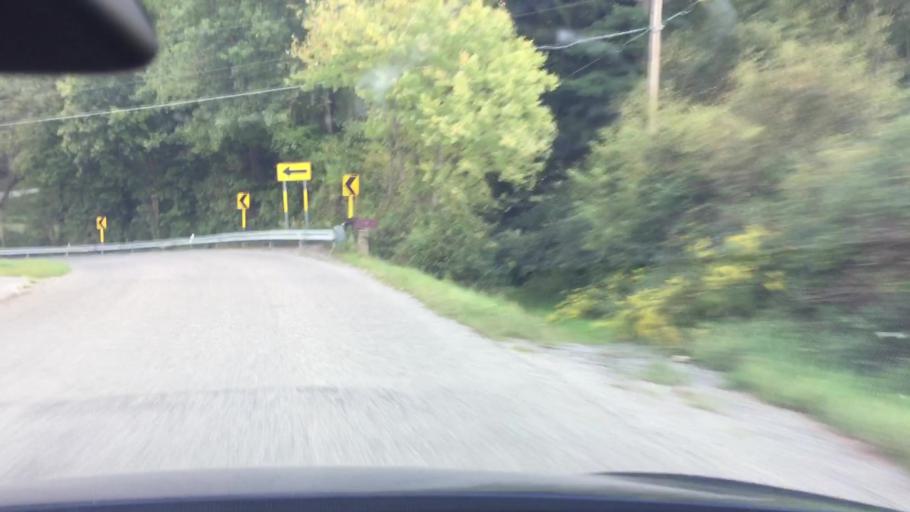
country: US
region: Pennsylvania
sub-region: Butler County
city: Oak Hills
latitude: 40.8106
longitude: -79.8915
